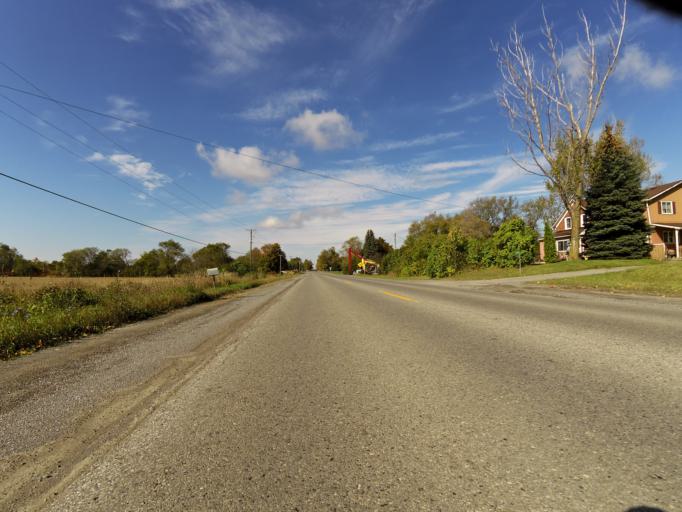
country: CA
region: Ontario
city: Prince Edward
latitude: 44.0025
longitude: -77.2195
